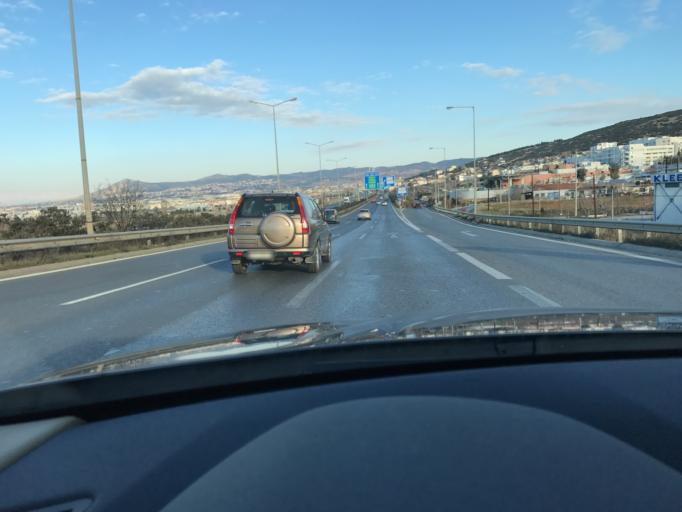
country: GR
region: Central Macedonia
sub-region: Nomos Thessalonikis
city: Polichni
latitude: 40.6699
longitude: 22.9619
